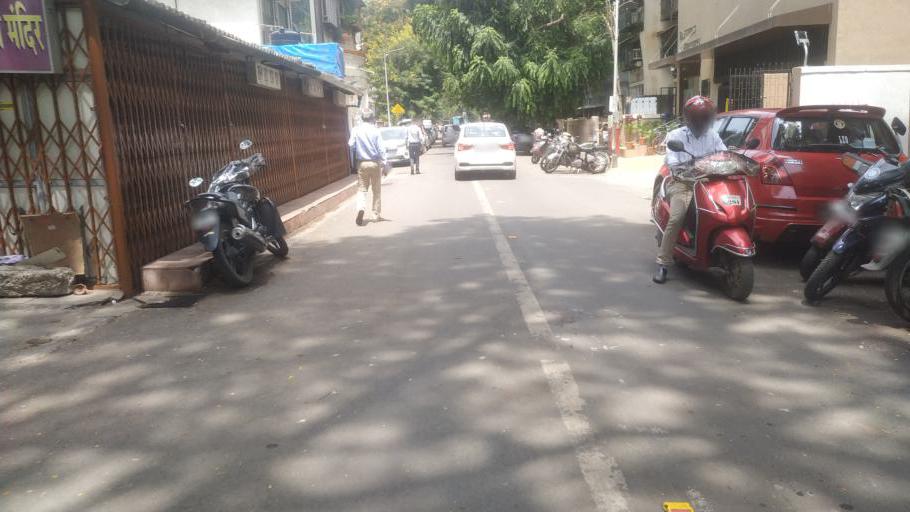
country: IN
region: Maharashtra
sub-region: Mumbai Suburban
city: Mumbai
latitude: 19.0178
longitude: 72.8357
